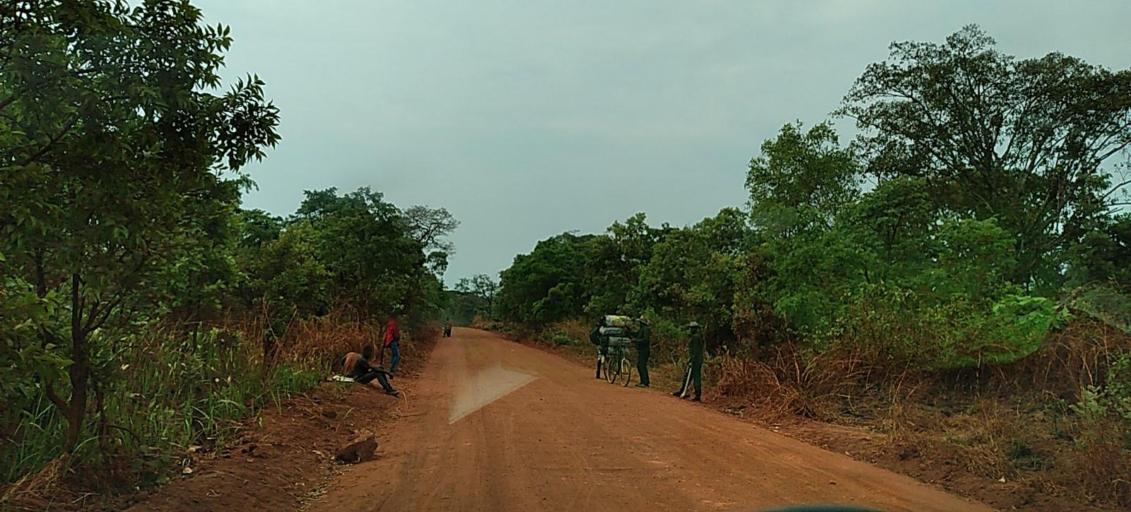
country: ZM
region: North-Western
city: Solwezi
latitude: -12.2196
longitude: 26.5095
